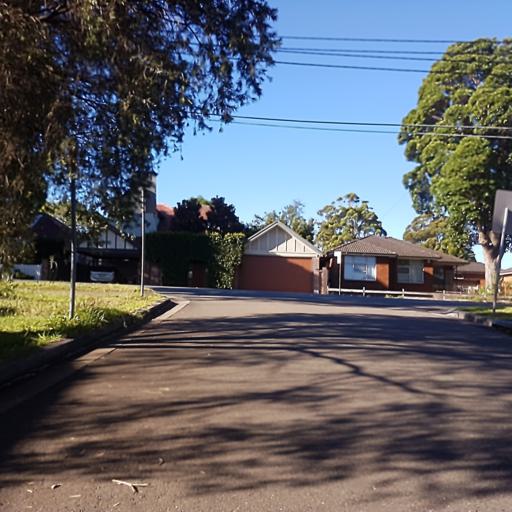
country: AU
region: New South Wales
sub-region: Willoughby
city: Castle Cove
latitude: -33.8044
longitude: 151.2035
